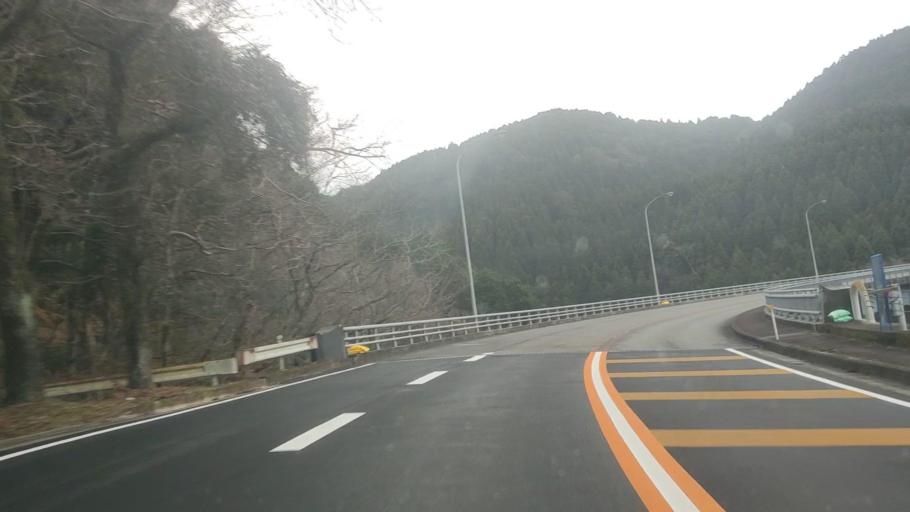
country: JP
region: Kumamoto
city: Hitoyoshi
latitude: 32.1198
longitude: 130.8150
